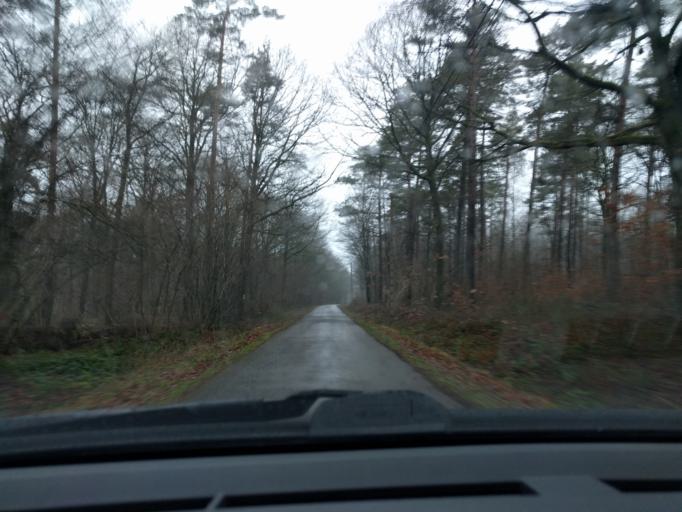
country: BE
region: Wallonia
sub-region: Province de Namur
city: Couvin
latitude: 50.0436
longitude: 4.5302
